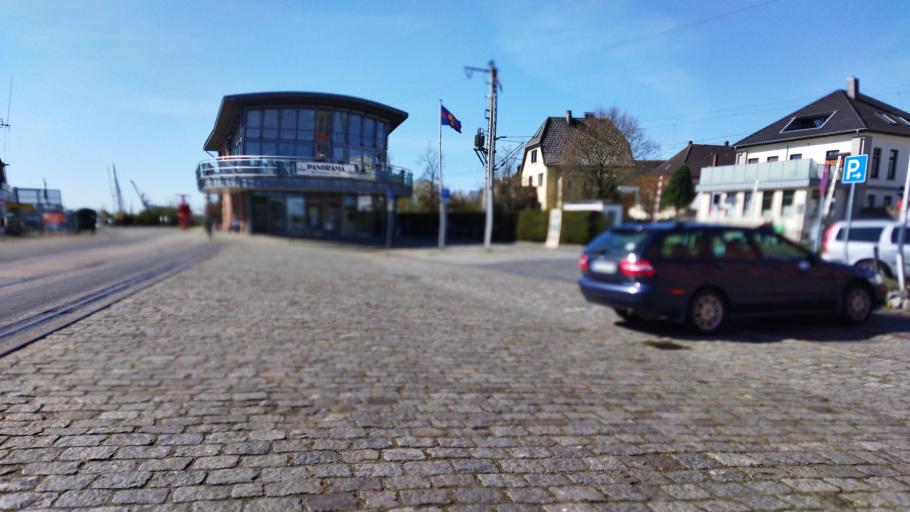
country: DE
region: Lower Saxony
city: Elsfleth
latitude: 53.2359
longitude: 8.4650
